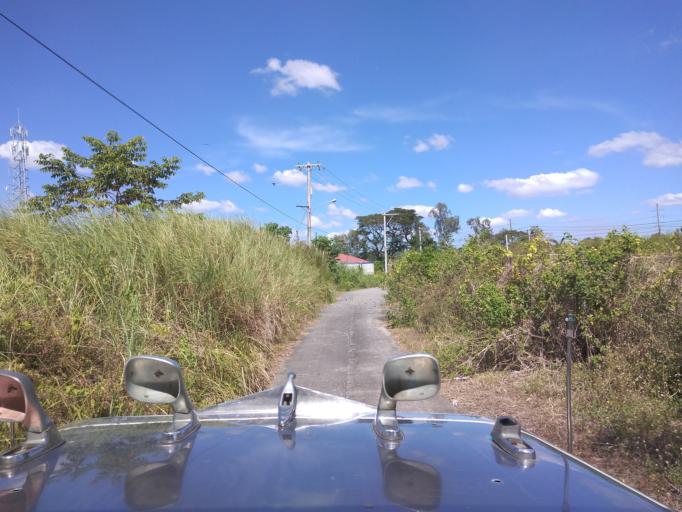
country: PH
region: Central Luzon
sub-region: Province of Pampanga
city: Calibutbut
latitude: 15.1139
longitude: 120.5960
